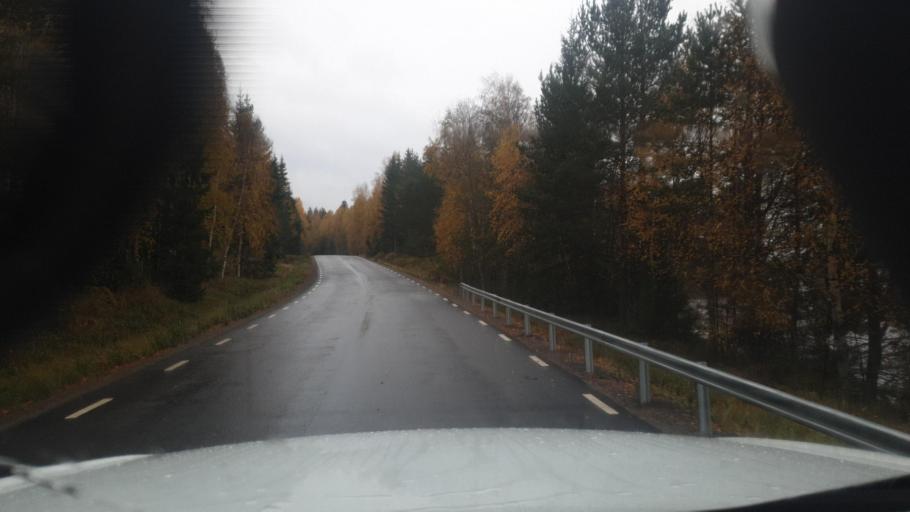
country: SE
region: Vaermland
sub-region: Torsby Kommun
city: Torsby
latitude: 60.0032
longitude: 12.7220
